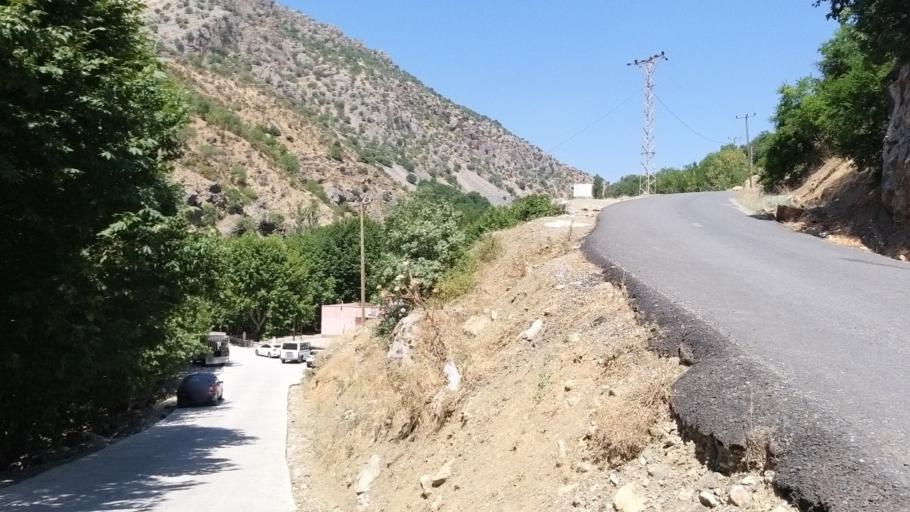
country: TR
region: Batman
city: Kozluk
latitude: 38.2180
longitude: 41.4849
